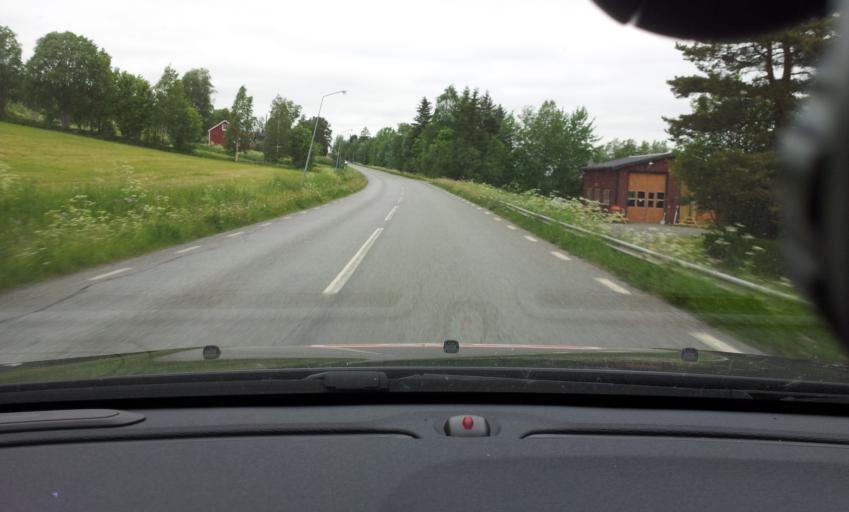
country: SE
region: Jaemtland
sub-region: Krokoms Kommun
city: Krokom
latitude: 63.1808
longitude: 14.0853
